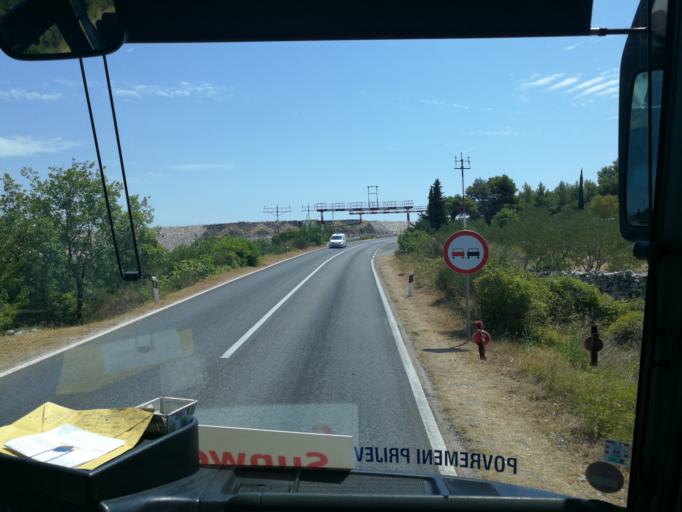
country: HR
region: Dubrovacko-Neretvanska
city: Cavtat
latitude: 42.5712
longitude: 18.2441
